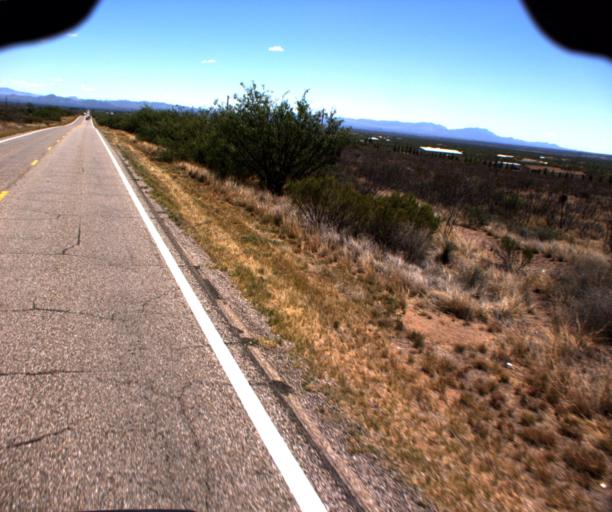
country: US
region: Arizona
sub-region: Cochise County
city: Huachuca City
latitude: 31.6918
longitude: -110.3941
